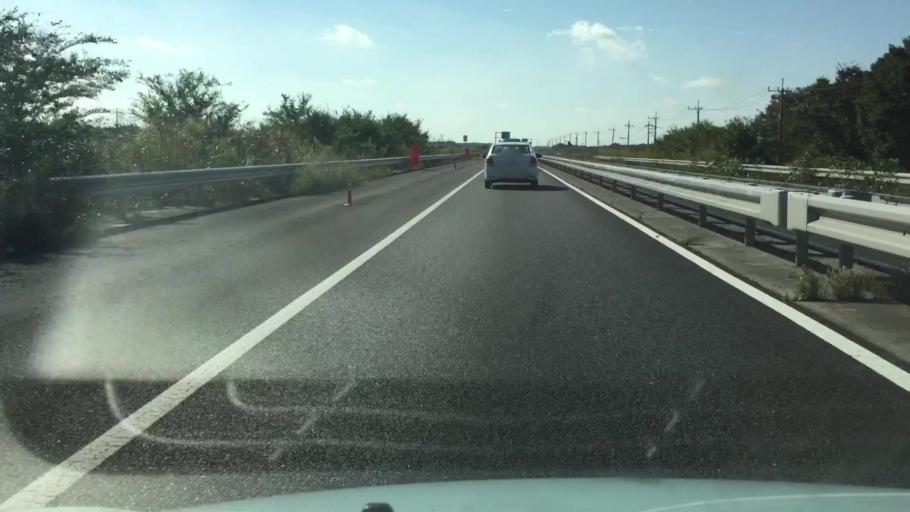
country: JP
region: Tochigi
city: Mooka
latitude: 36.5210
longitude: 139.9848
